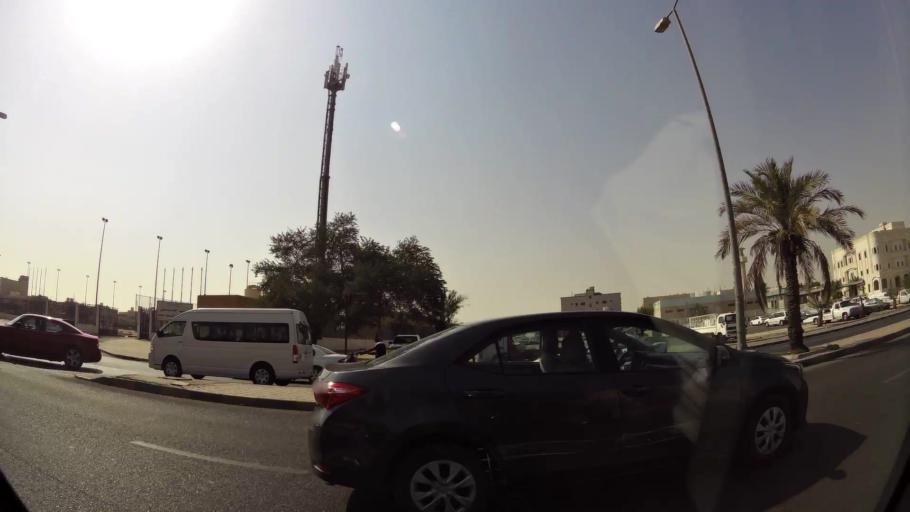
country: KW
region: Al Ahmadi
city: Al Fahahil
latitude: 29.0798
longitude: 48.1236
